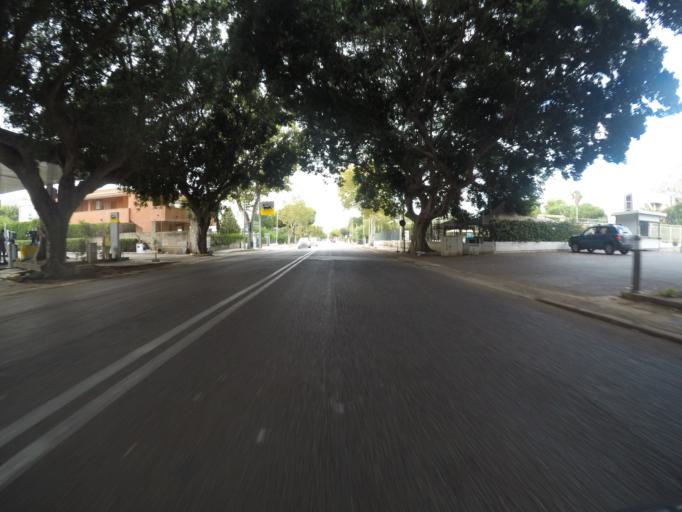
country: IT
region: Sicily
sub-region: Palermo
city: Palermo
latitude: 38.1907
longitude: 13.3327
